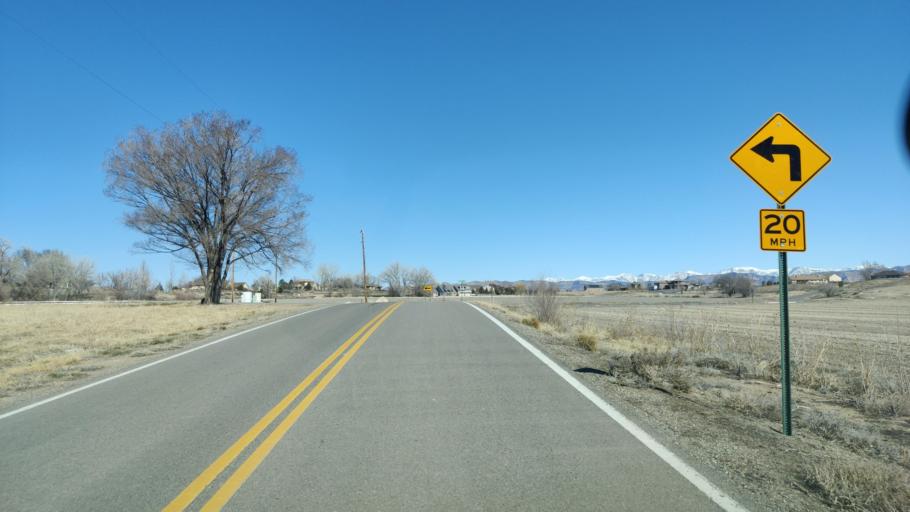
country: US
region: Colorado
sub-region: Mesa County
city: Fruita
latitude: 39.2031
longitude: -108.7105
